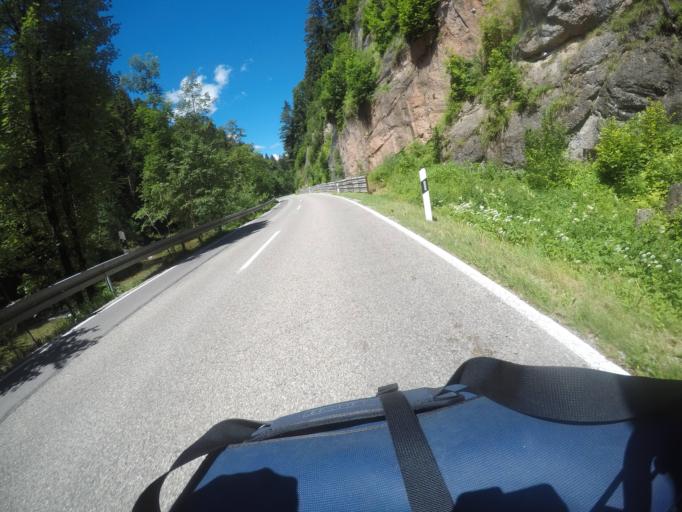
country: DE
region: Bavaria
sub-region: Upper Bavaria
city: Prem
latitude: 47.6533
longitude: 10.7910
